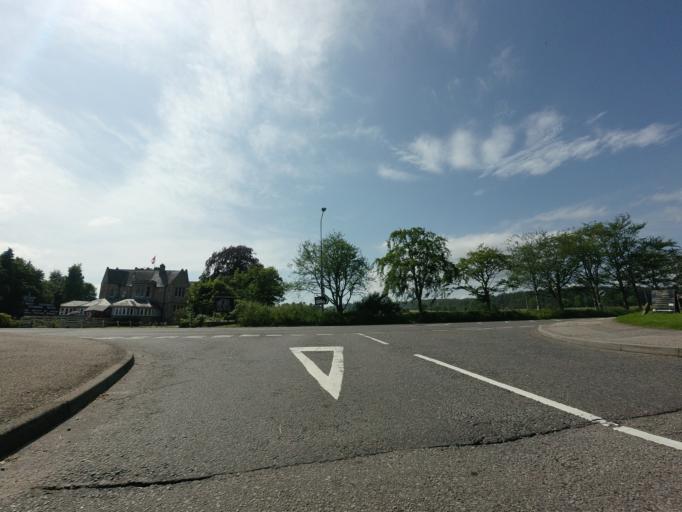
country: GB
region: Scotland
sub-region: Highland
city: Tain
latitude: 57.8167
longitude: -4.0665
